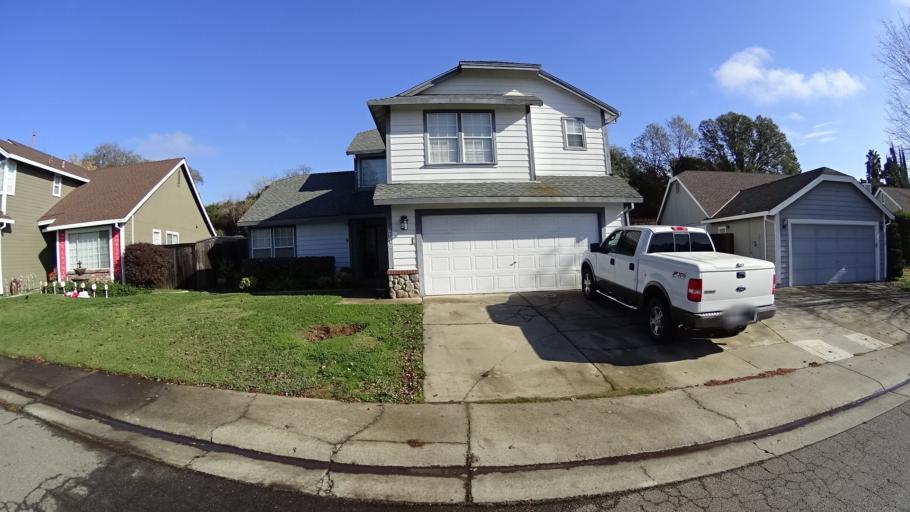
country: US
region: California
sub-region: Sacramento County
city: Antelope
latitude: 38.6886
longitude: -121.3274
